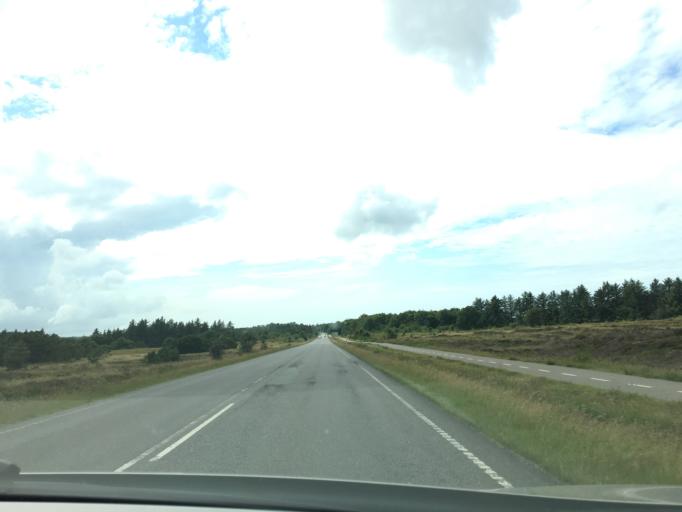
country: DK
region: South Denmark
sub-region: Varde Kommune
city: Oksbol
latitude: 55.7255
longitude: 8.2588
